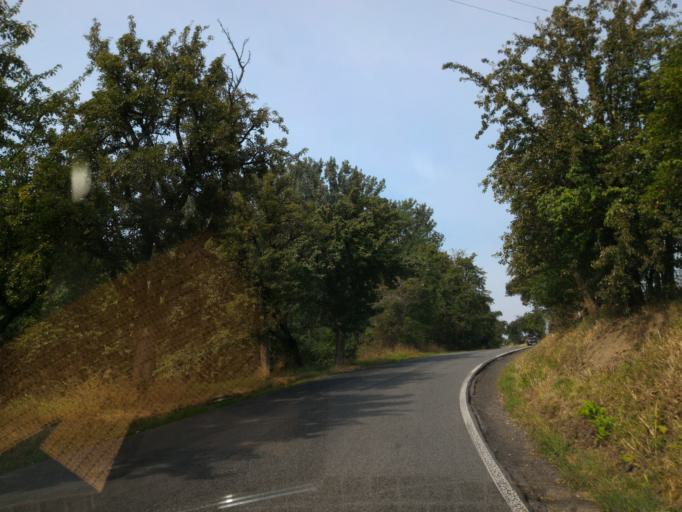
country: CZ
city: Prisovice
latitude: 50.5763
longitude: 15.0605
